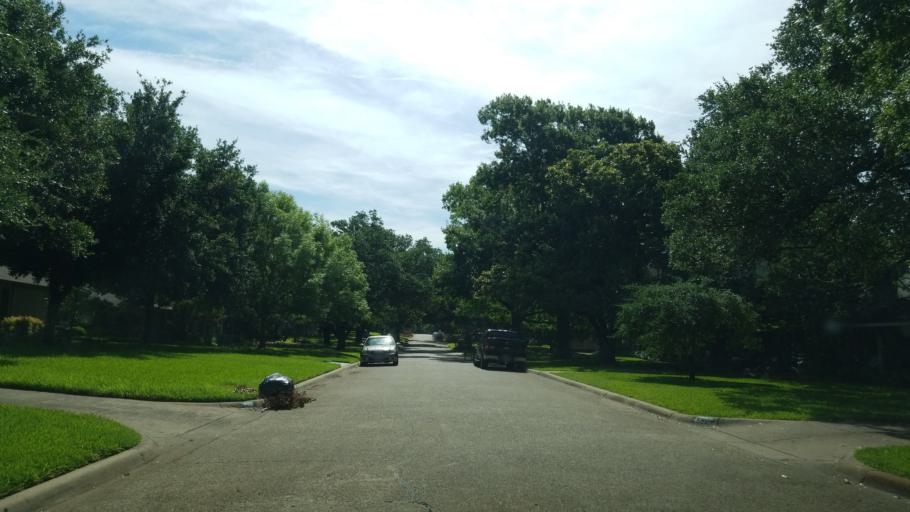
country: US
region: Texas
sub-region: Dallas County
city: Addison
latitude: 32.9081
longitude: -96.8354
